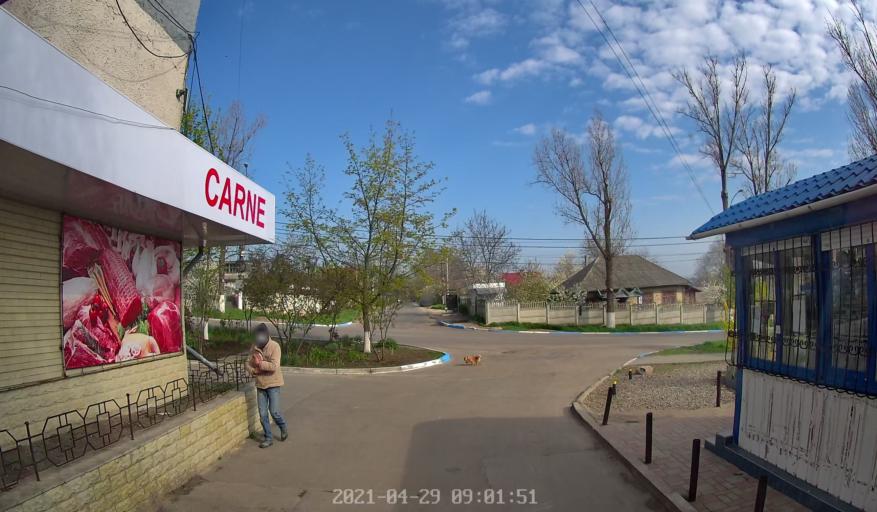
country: MD
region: Chisinau
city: Cricova
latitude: 47.1375
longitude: 28.8597
